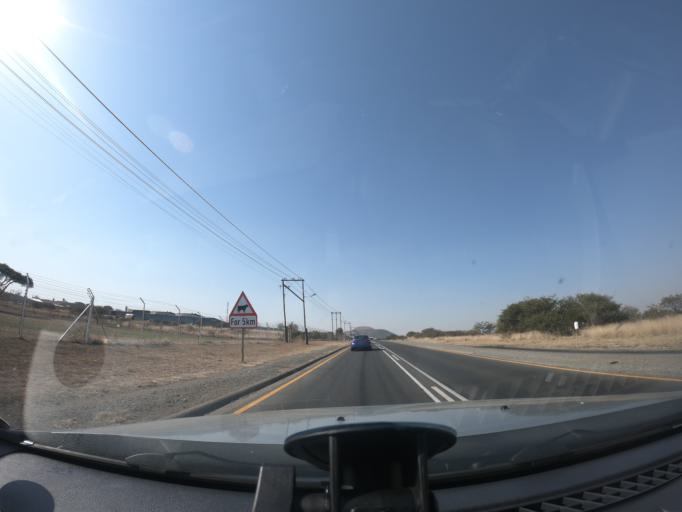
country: ZA
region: KwaZulu-Natal
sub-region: uThukela District Municipality
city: Ladysmith
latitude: -28.5440
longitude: 29.8108
